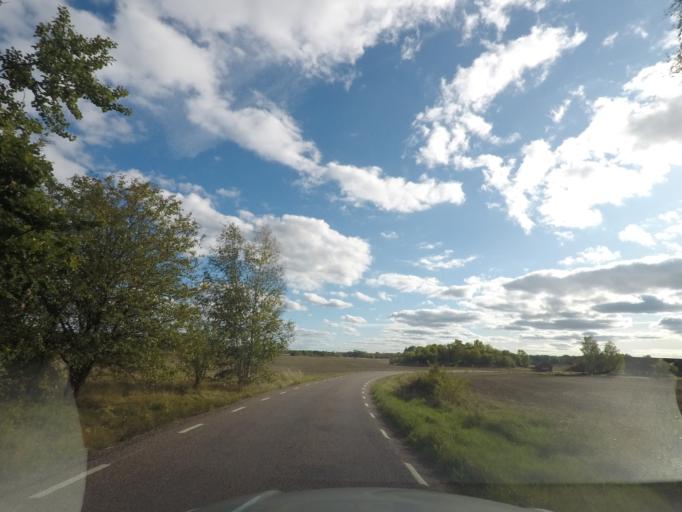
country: SE
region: Vaestmanland
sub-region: Hallstahammars Kommun
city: Kolback
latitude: 59.5170
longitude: 16.1885
